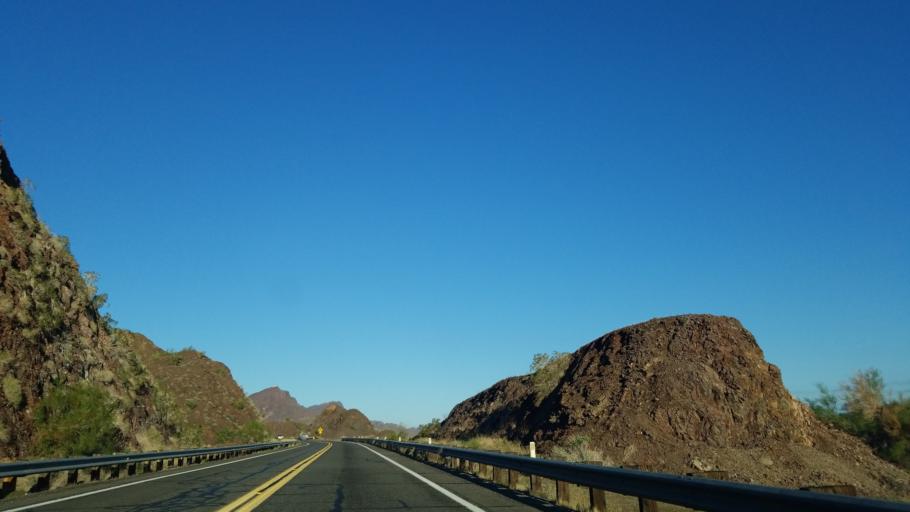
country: US
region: Arizona
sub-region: La Paz County
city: Cienega Springs
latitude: 34.2901
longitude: -114.1129
